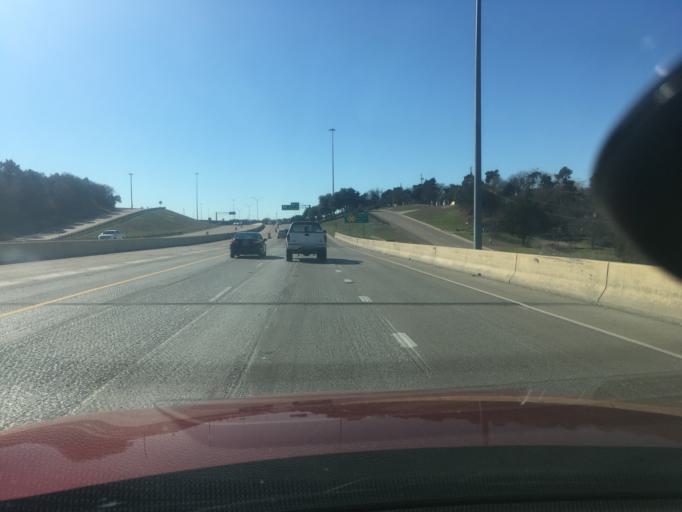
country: US
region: Texas
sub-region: Dallas County
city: Cockrell Hill
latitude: 32.6961
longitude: -96.8428
